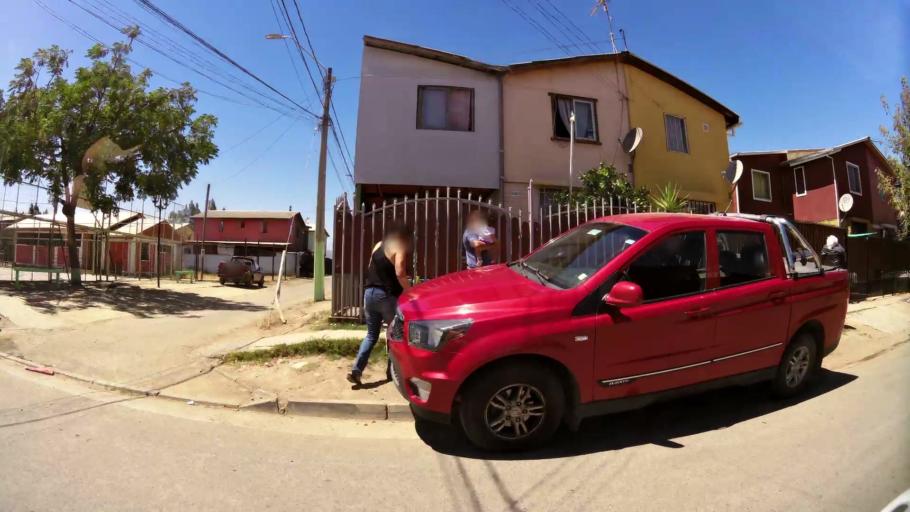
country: CL
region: O'Higgins
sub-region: Provincia de Cachapoal
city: Rancagua
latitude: -34.1498
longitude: -70.7175
